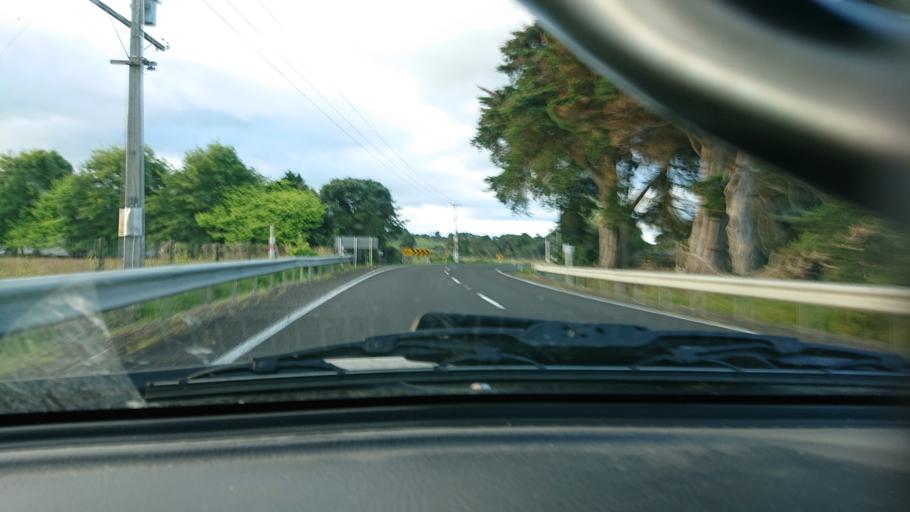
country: NZ
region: Auckland
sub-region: Auckland
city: Parakai
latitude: -36.4963
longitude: 174.4490
